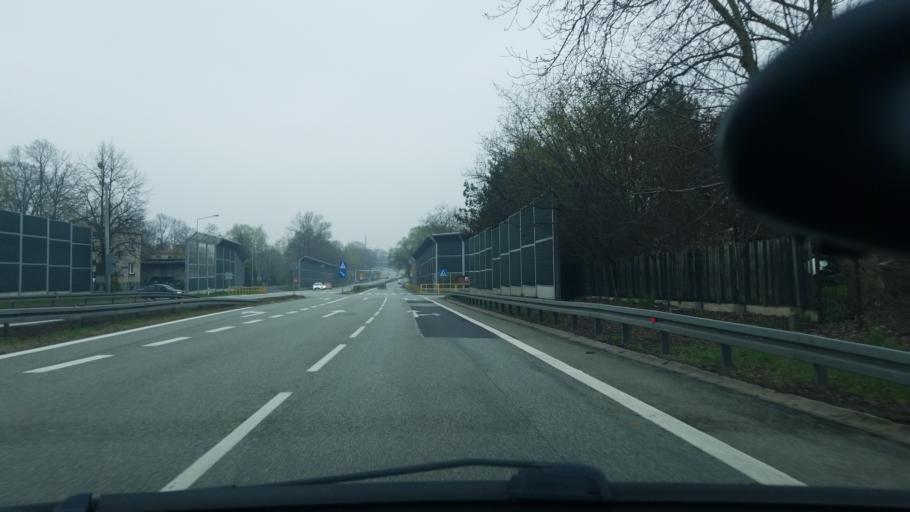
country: PL
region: Silesian Voivodeship
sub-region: Powiat pszczynski
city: Pawlowice
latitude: 49.9970
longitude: 18.7114
